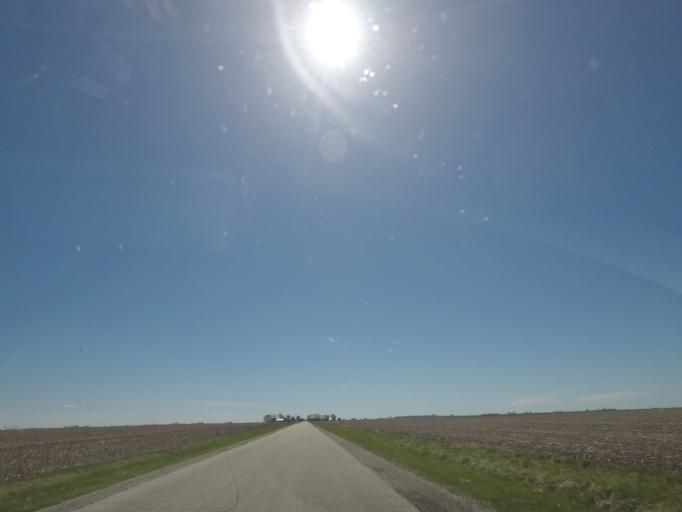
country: US
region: Illinois
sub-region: Logan County
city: Atlanta
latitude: 40.1917
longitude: -89.1941
